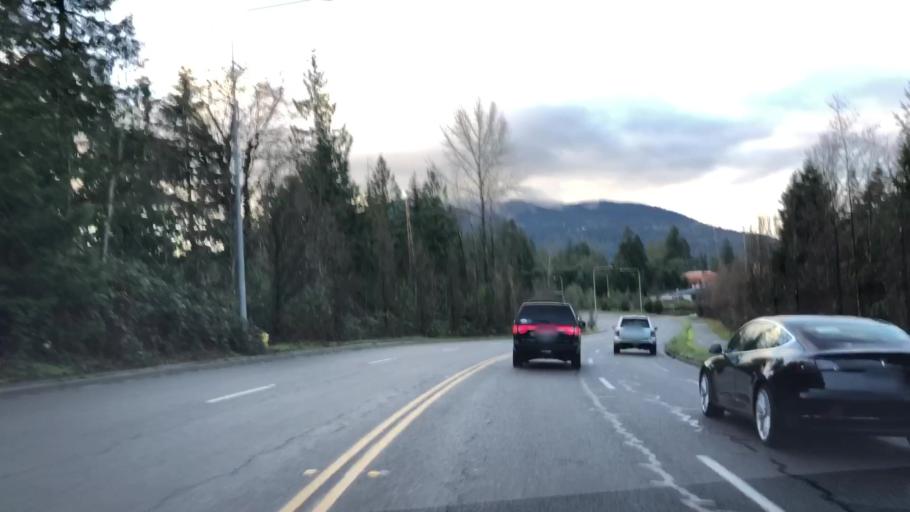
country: US
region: Washington
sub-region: King County
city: Issaquah
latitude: 47.5524
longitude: -122.0211
